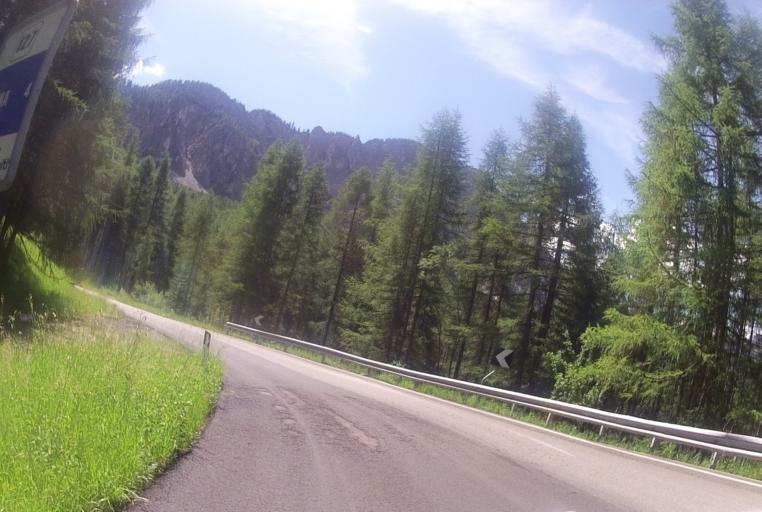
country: IT
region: Veneto
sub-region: Provincia di Belluno
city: Cortina d'Ampezzo
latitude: 46.5475
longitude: 12.1662
